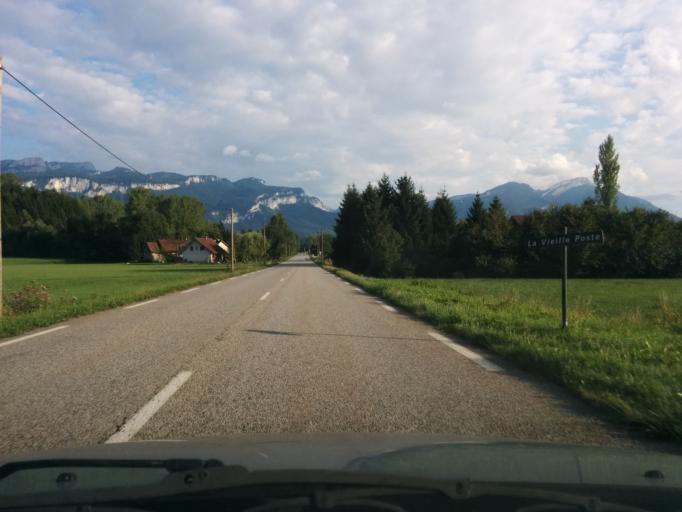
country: FR
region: Rhone-Alpes
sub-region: Departement de la Savoie
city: Les Echelles
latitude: 45.4520
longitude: 5.7364
